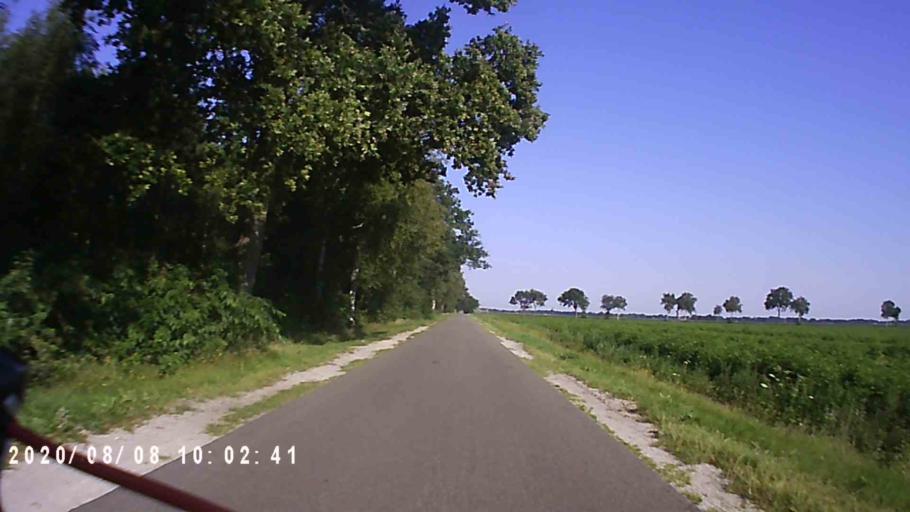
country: NL
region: Groningen
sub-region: Gemeente Leek
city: Leek
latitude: 53.1067
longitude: 6.3846
